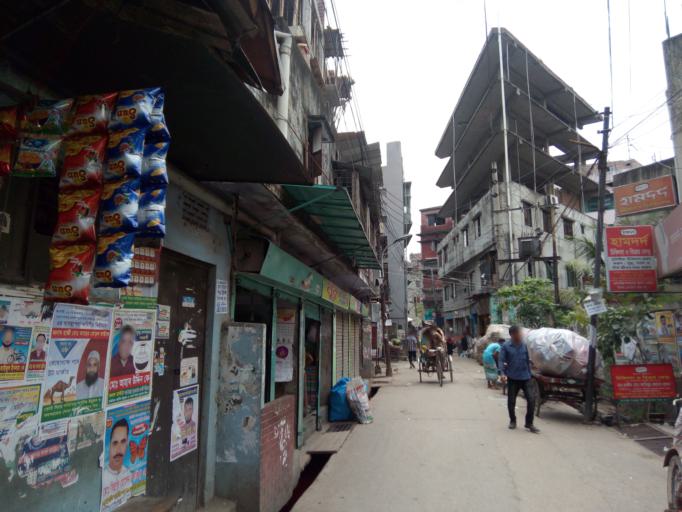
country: BD
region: Dhaka
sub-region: Dhaka
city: Dhaka
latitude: 23.7232
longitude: 90.4023
